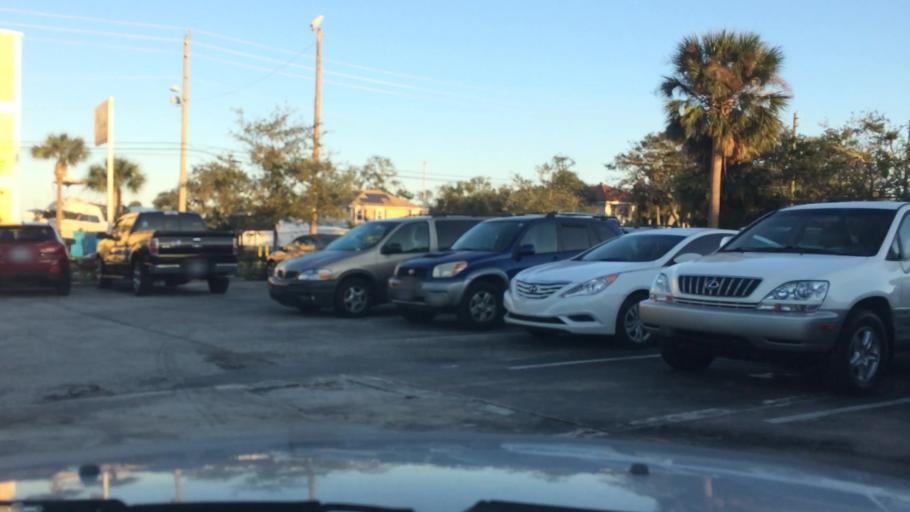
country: US
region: Florida
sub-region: Volusia County
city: Daytona Beach
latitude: 29.2256
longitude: -81.0238
